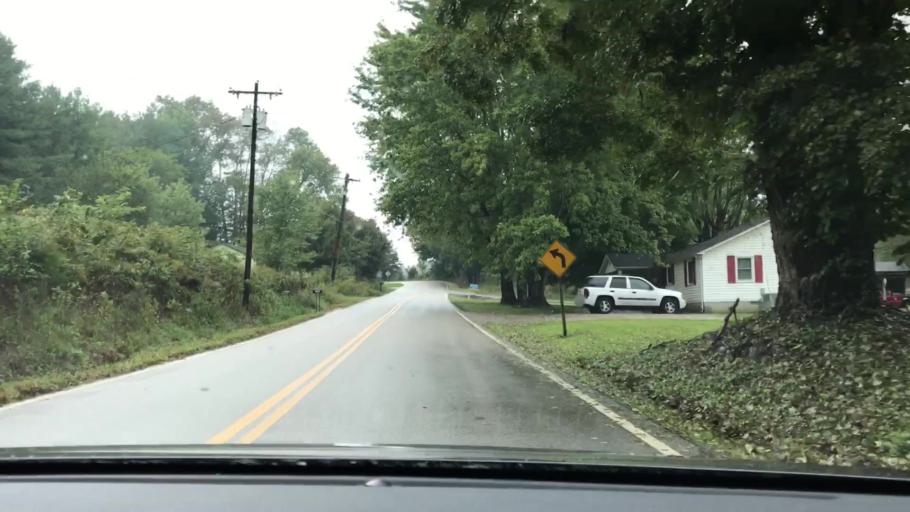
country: US
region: Tennessee
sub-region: Macon County
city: Red Boiling Springs
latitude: 36.4320
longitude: -85.8962
